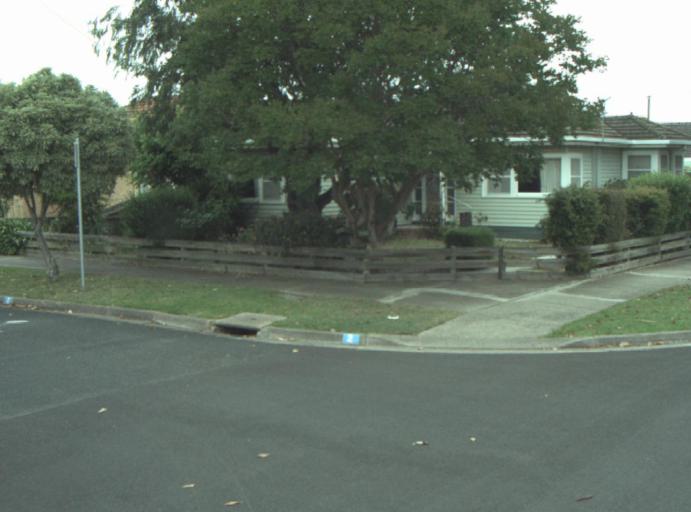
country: AU
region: Victoria
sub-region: Greater Geelong
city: Hamlyn Heights
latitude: -38.1325
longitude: 144.3296
